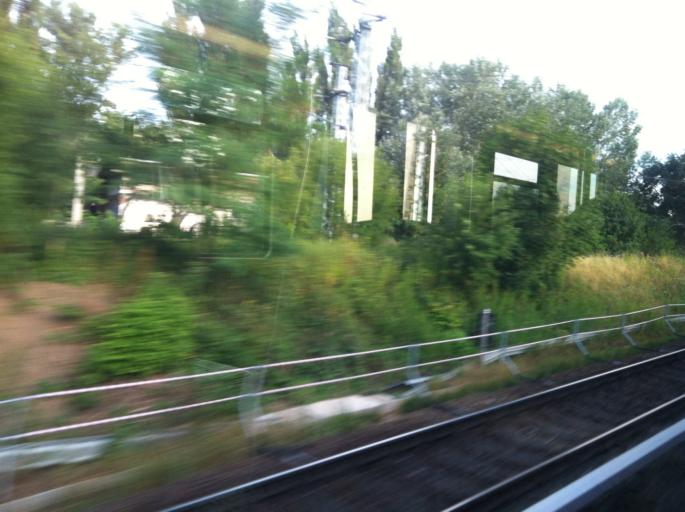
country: DE
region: Berlin
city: Blankenburg
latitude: 52.6082
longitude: 13.4612
